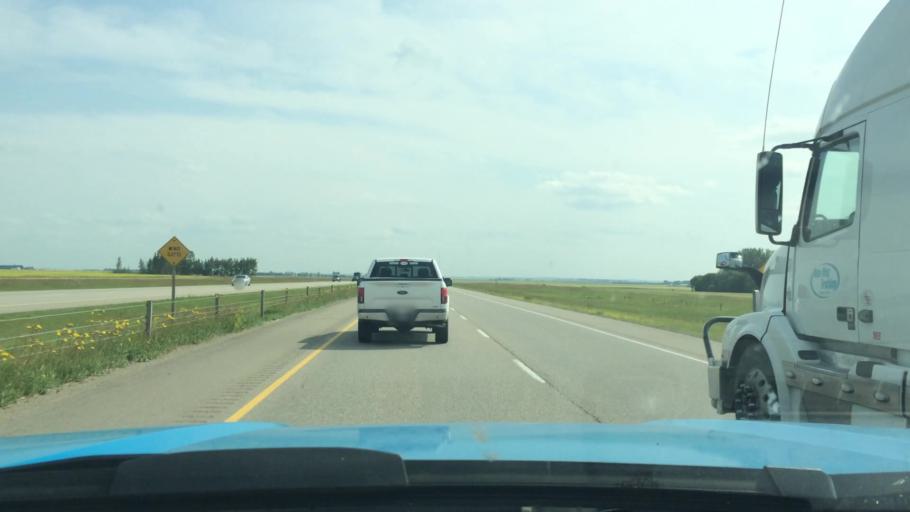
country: CA
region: Alberta
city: Didsbury
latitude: 51.6534
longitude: -114.0256
